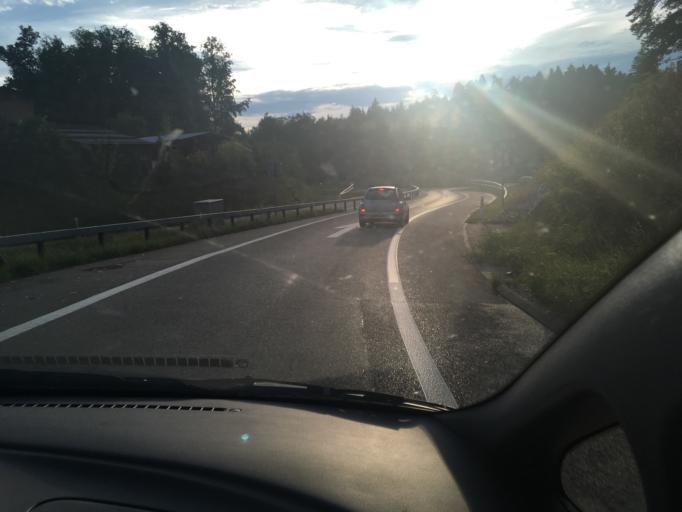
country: CH
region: Bern
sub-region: Bern-Mittelland District
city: Bern
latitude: 46.9666
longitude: 7.4310
